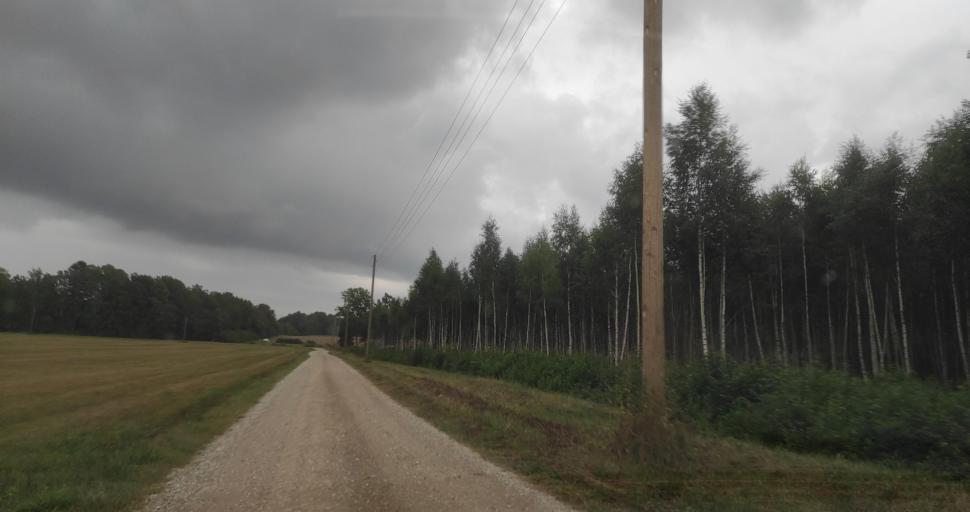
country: LV
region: Durbe
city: Liegi
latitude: 56.7037
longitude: 21.3620
